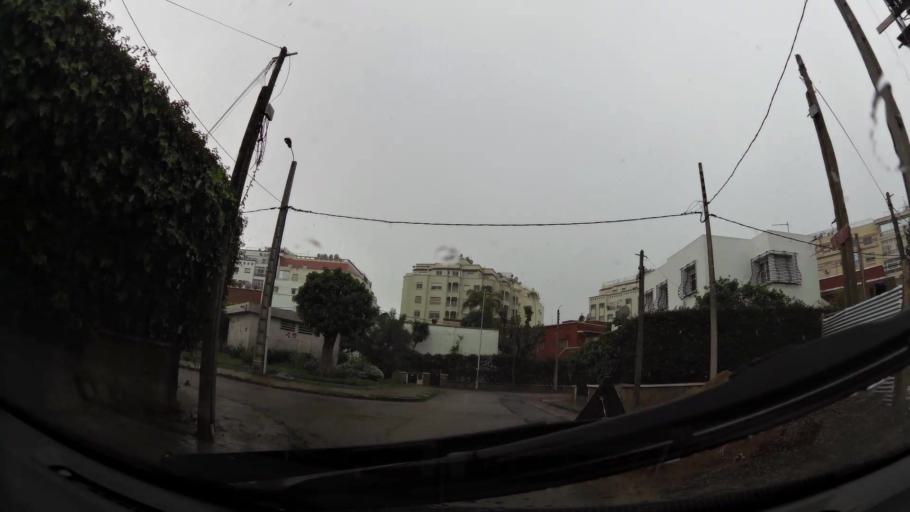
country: MA
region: Grand Casablanca
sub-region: Casablanca
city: Casablanca
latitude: 33.5735
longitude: -7.6300
